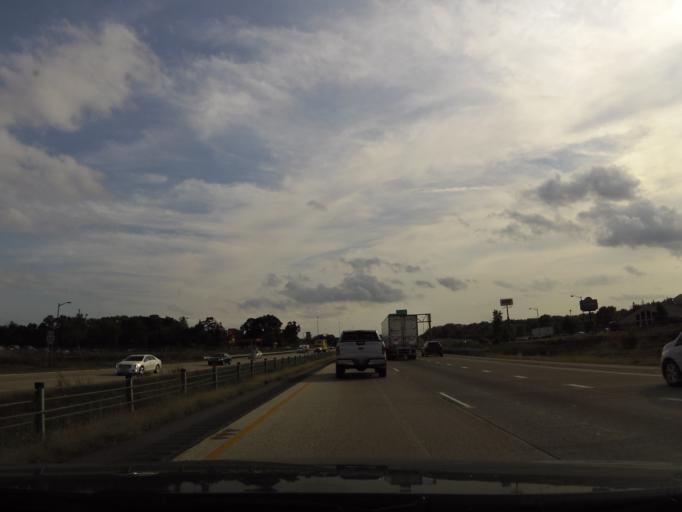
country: US
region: Minnesota
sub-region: Dakota County
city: Burnsville
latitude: 44.7022
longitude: -93.2861
